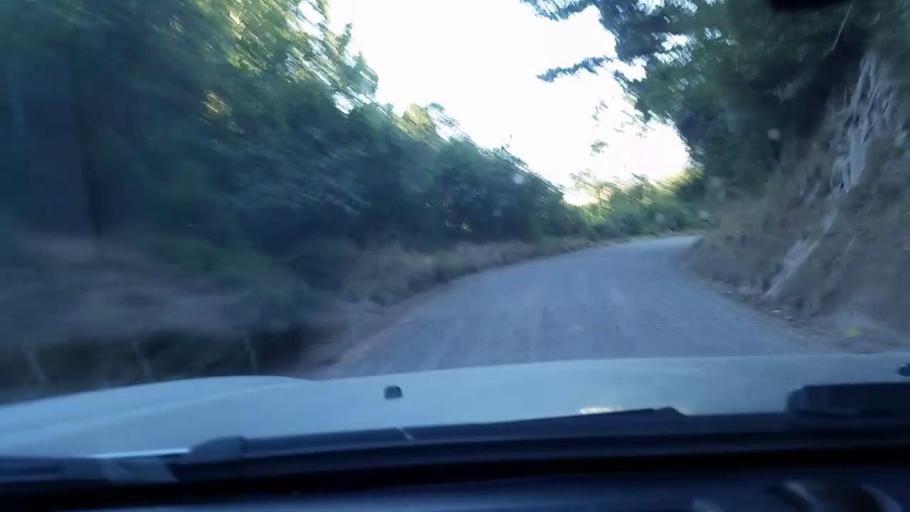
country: NZ
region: Bay of Plenty
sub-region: Rotorua District
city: Rotorua
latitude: -38.3885
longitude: 176.1704
